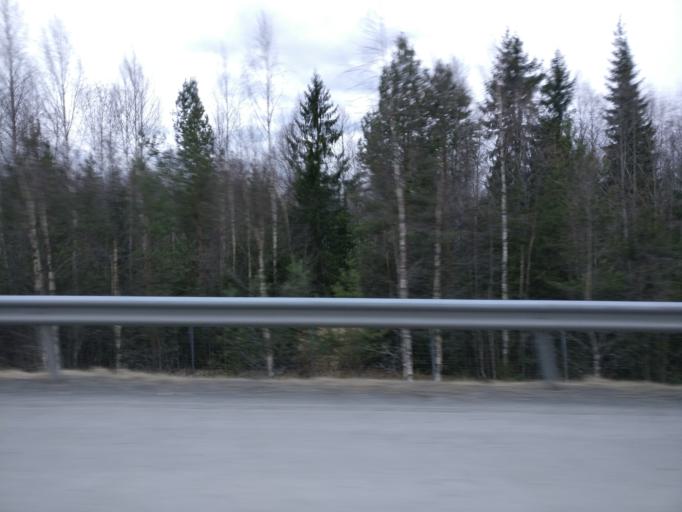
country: FI
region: Haeme
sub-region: Haemeenlinna
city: Kalvola
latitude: 61.1272
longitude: 24.1121
